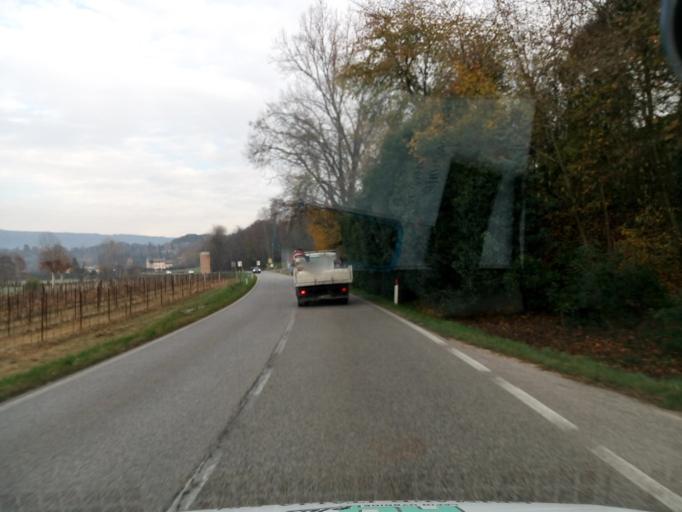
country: IT
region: Veneto
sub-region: Provincia di Treviso
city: Asolo
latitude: 45.7943
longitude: 11.8977
